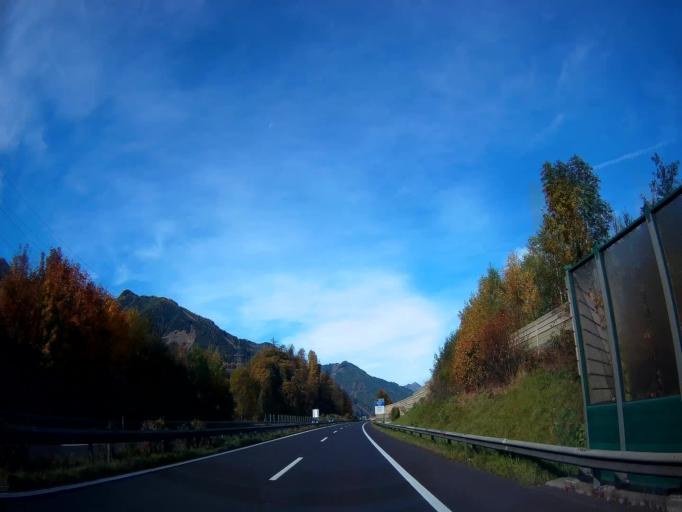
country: AT
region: Styria
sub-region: Politischer Bezirk Leoben
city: Mautern in Steiermark
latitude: 47.3949
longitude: 14.8304
